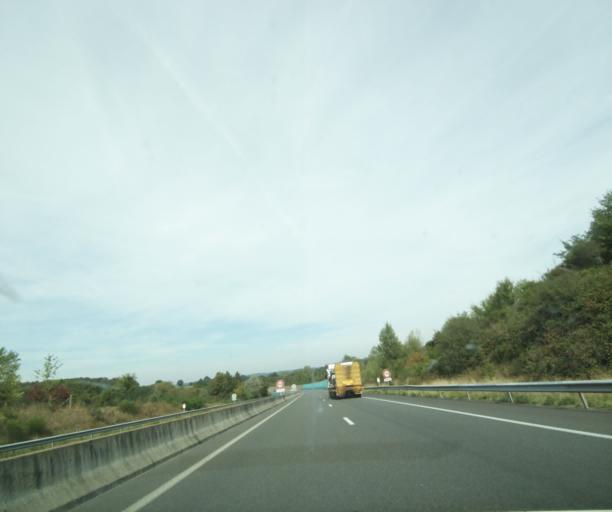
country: FR
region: Auvergne
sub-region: Departement de l'Allier
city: Lapalisse
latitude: 46.2292
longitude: 3.6497
